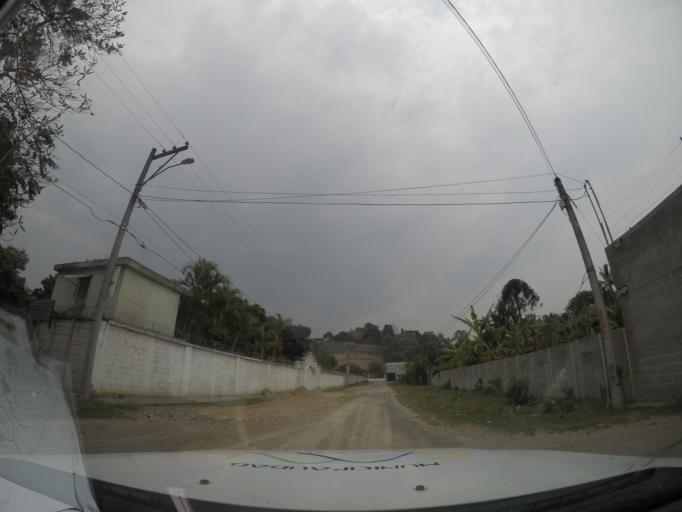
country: GT
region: Guatemala
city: Petapa
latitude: 14.5085
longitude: -90.5509
